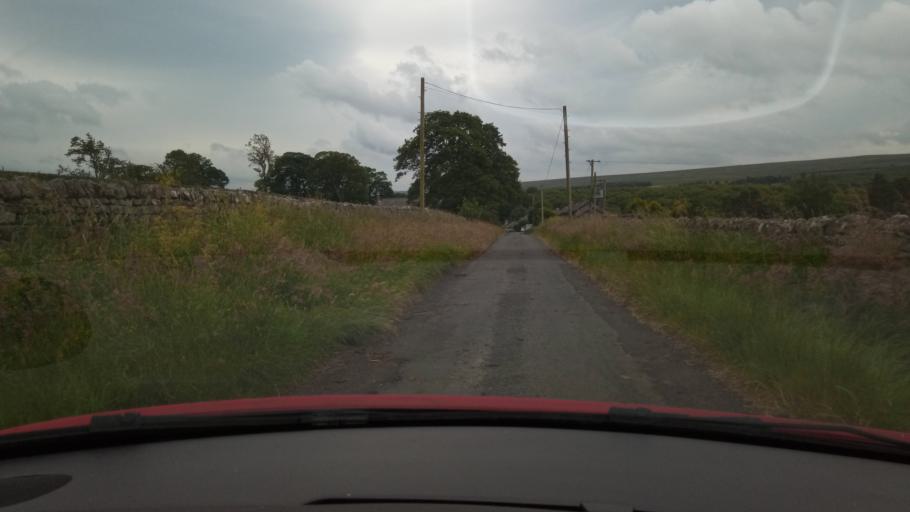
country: GB
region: England
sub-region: Northumberland
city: Rochester
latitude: 55.2789
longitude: -2.2651
